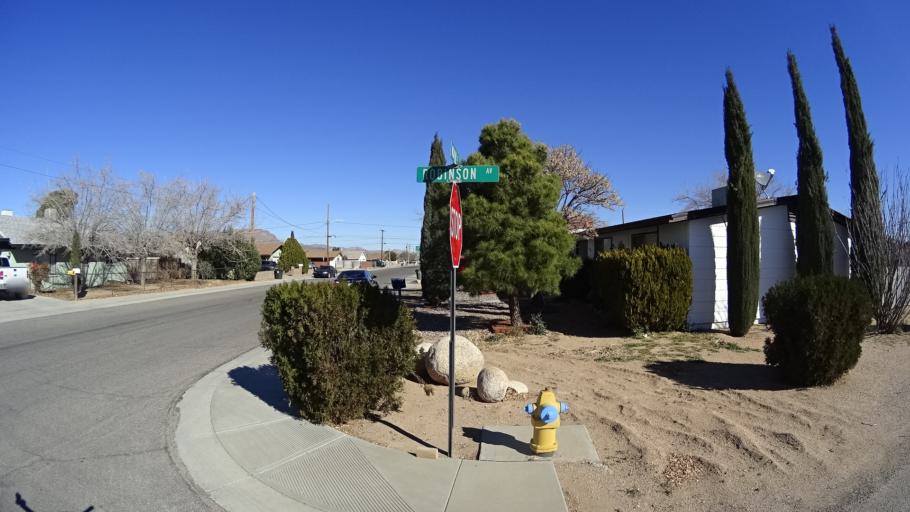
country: US
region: Arizona
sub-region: Mohave County
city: Kingman
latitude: 35.2053
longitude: -114.0312
